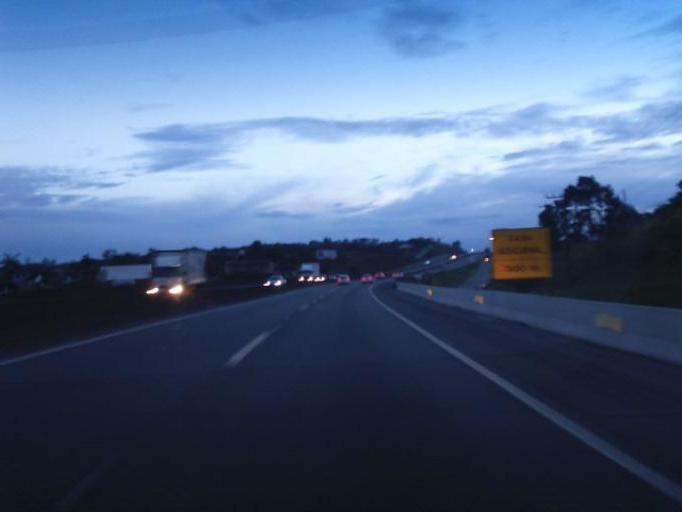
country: BR
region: Santa Catarina
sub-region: Joinville
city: Joinville
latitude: -26.3472
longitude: -48.8573
